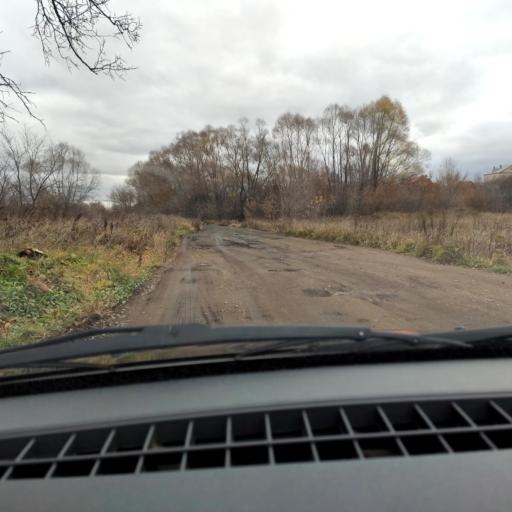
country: RU
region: Bashkortostan
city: Avdon
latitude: 54.4900
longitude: 55.8510
